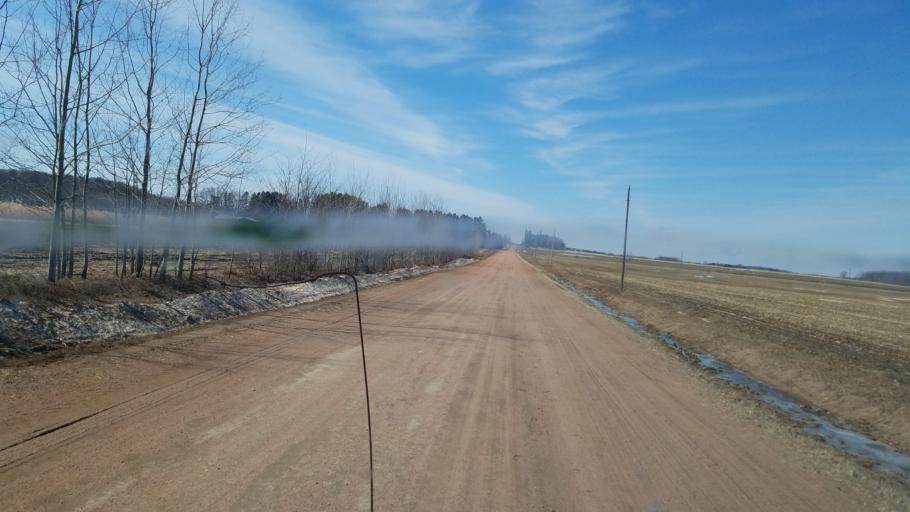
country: US
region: Wisconsin
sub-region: Clark County
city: Loyal
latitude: 44.6111
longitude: -90.4299
